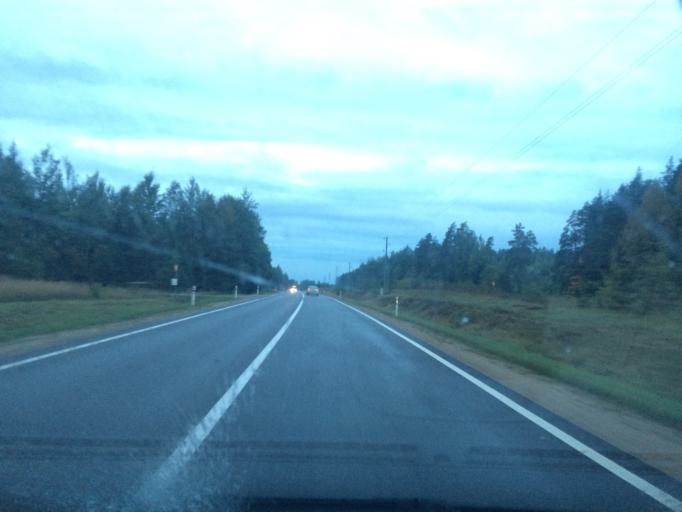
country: LV
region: Jekabpils Rajons
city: Jekabpils
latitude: 56.5378
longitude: 26.0491
